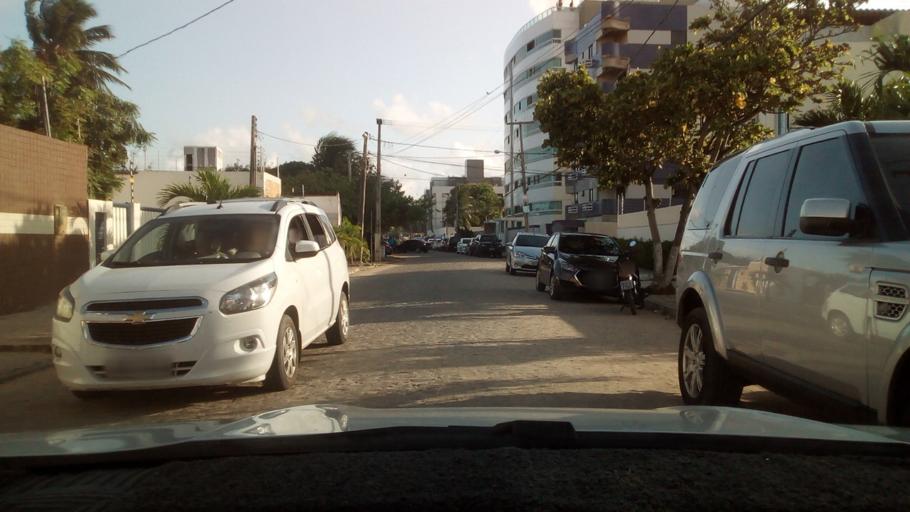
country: BR
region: Paraiba
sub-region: Cabedelo
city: Cabedelo
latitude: -7.0162
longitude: -34.8296
